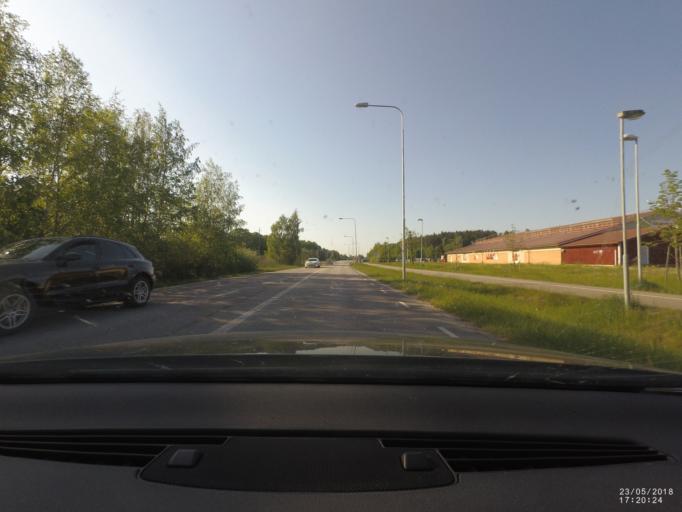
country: SE
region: Soedermanland
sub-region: Nykopings Kommun
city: Nykoping
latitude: 58.7286
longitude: 17.0122
